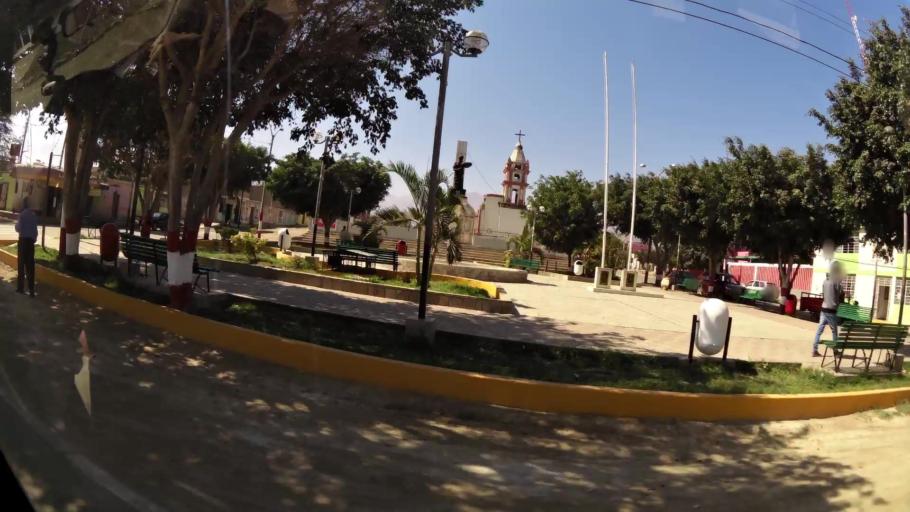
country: PE
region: Ica
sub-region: Provincia de Ica
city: San Juan Bautista
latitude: -13.9329
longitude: -75.6711
